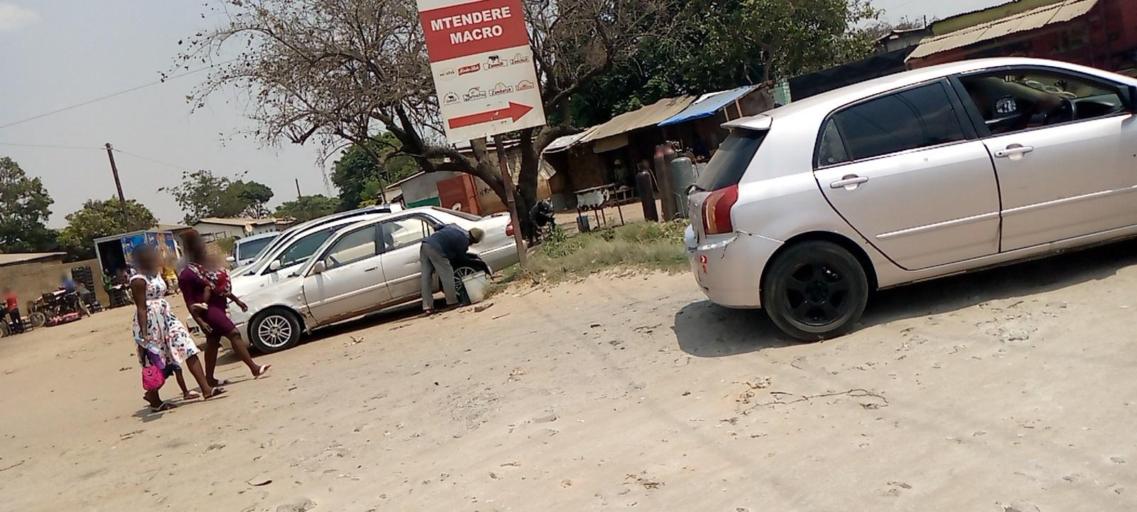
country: ZM
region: Lusaka
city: Lusaka
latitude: -15.4032
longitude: 28.3488
